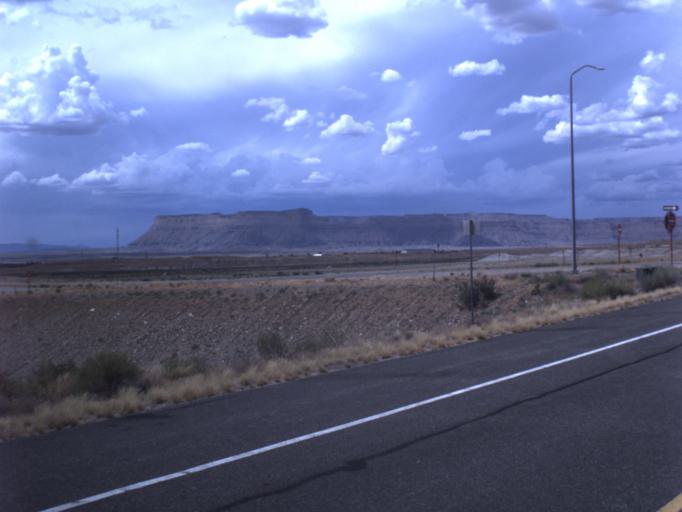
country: US
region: Utah
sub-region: Carbon County
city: East Carbon City
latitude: 38.9750
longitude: -110.1214
